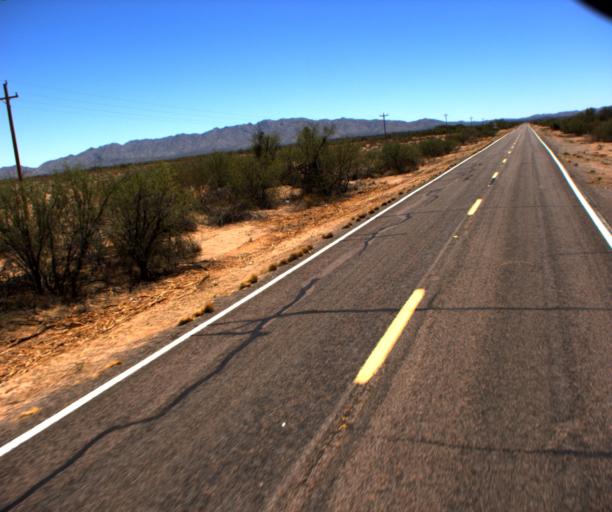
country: US
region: Arizona
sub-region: Pima County
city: Sells
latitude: 32.1824
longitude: -112.3442
